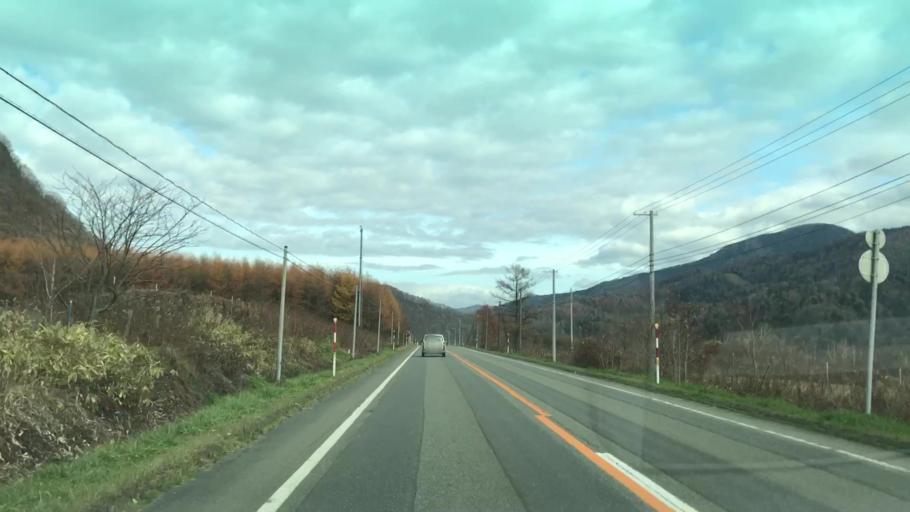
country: JP
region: Hokkaido
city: Shizunai-furukawacho
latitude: 42.7790
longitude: 142.3894
